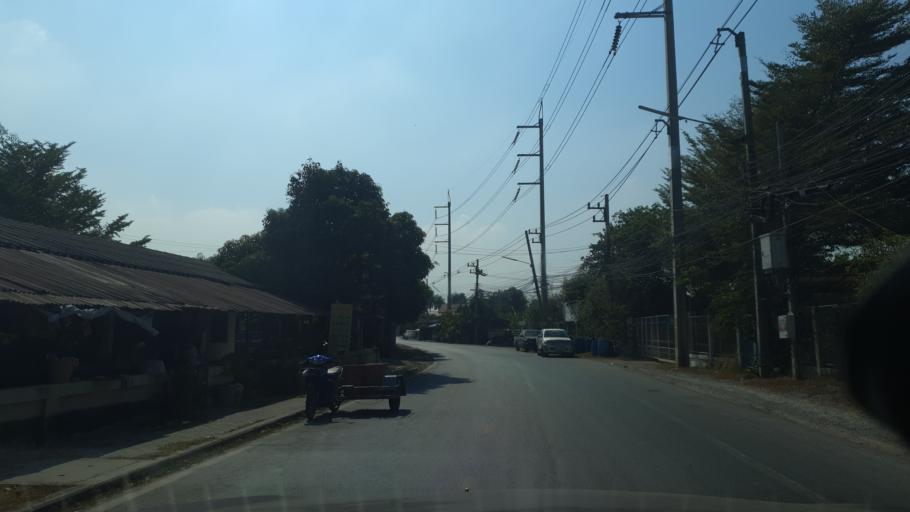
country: TH
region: Nakhon Pathom
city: Salaya
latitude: 13.7809
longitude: 100.2696
